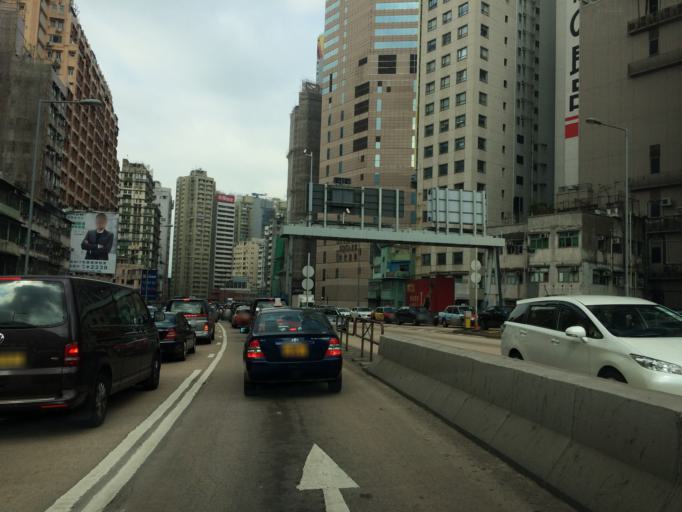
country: HK
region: Wanchai
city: Wan Chai
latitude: 22.2768
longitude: 114.1811
